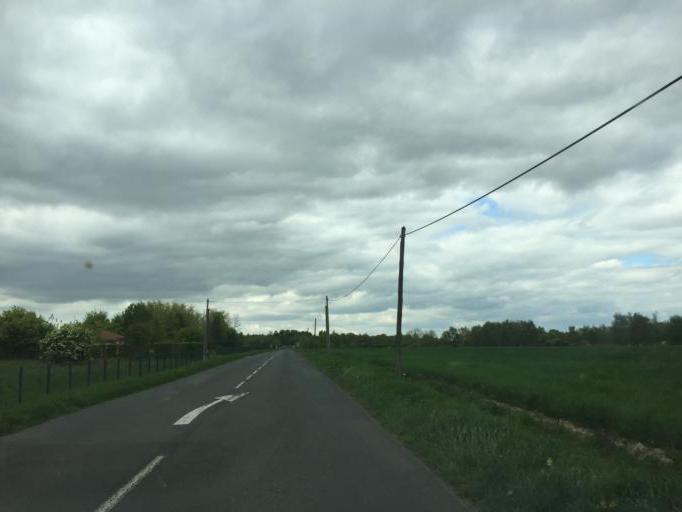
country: FR
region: Rhone-Alpes
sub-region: Departement de l'Ain
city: Saint-Andre-de-Corcy
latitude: 45.9638
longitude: 4.9392
